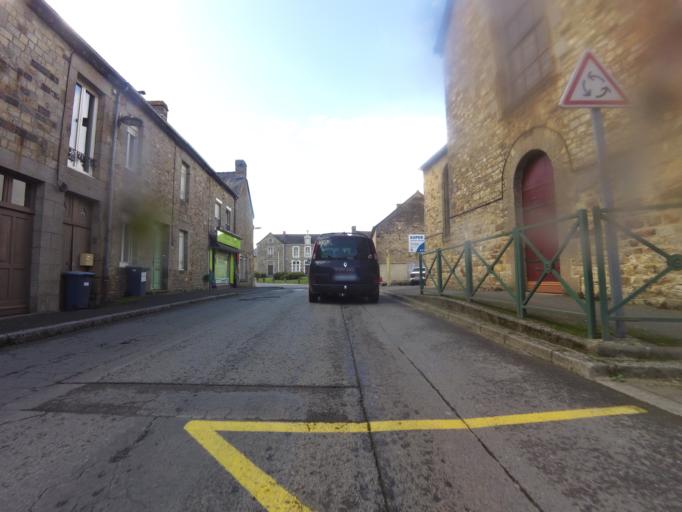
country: FR
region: Brittany
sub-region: Departement d'Ille-et-Vilaine
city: Erce-pres-Liffre
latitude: 48.2560
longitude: -1.5162
